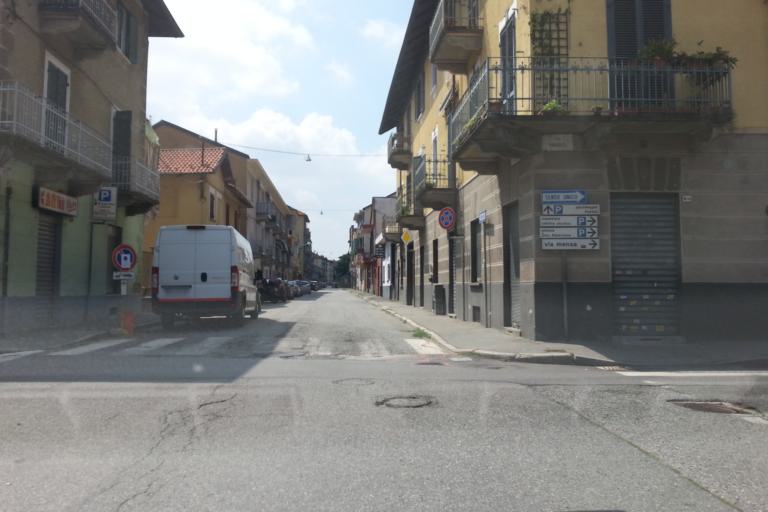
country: IT
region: Piedmont
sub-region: Provincia di Torino
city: Venaria Reale
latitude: 45.1312
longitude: 7.6326
